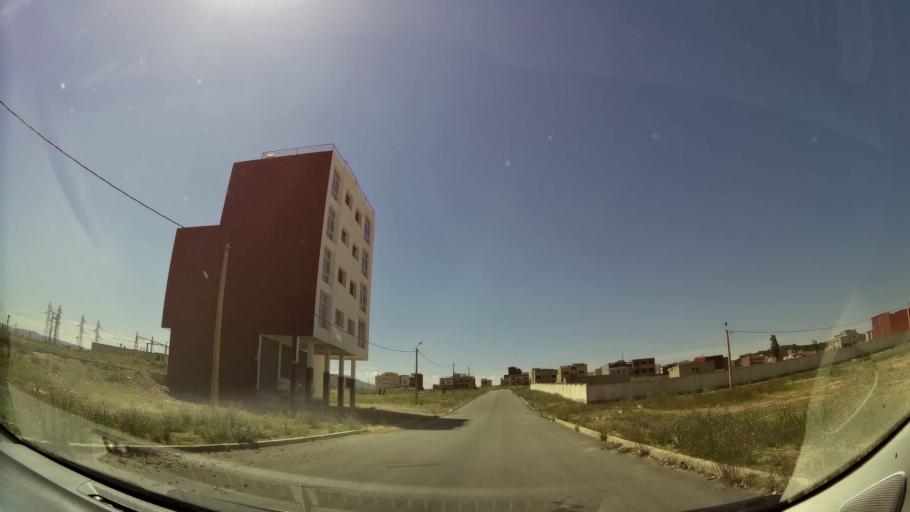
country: MA
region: Oriental
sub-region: Oujda-Angad
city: Oujda
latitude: 34.6565
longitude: -1.8711
